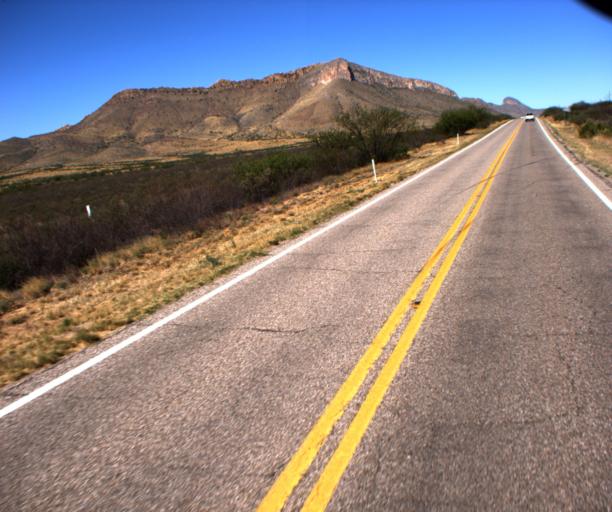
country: US
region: Arizona
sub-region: Cochise County
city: Huachuca City
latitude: 31.6921
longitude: -110.4033
